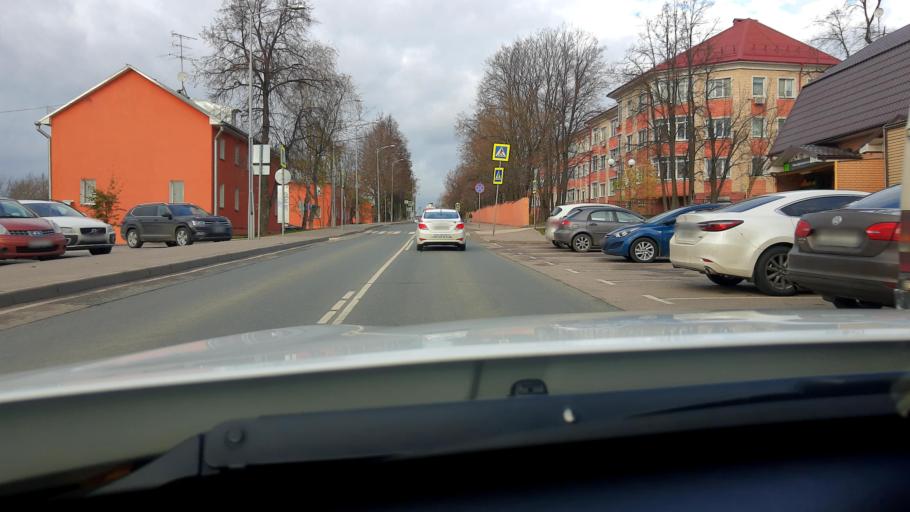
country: RU
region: Moskovskaya
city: Kokoshkino
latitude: 55.5361
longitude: 37.1527
